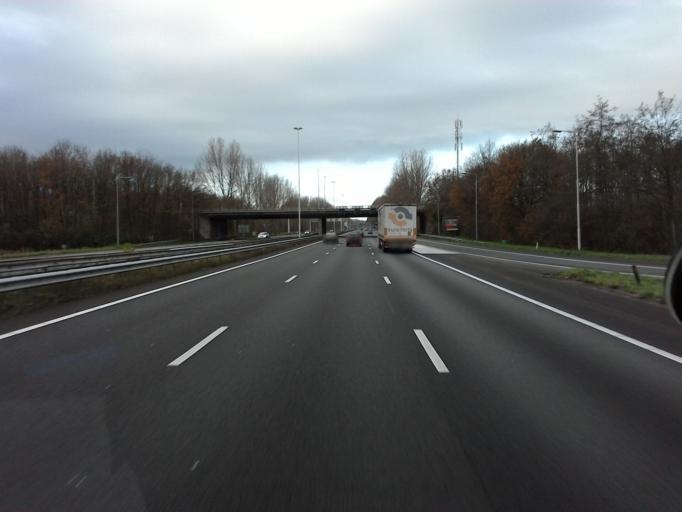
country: NL
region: South Holland
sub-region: Gemeente Krimpen aan den IJssel
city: Krimpen aan den IJssel
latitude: 51.9809
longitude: 4.6200
